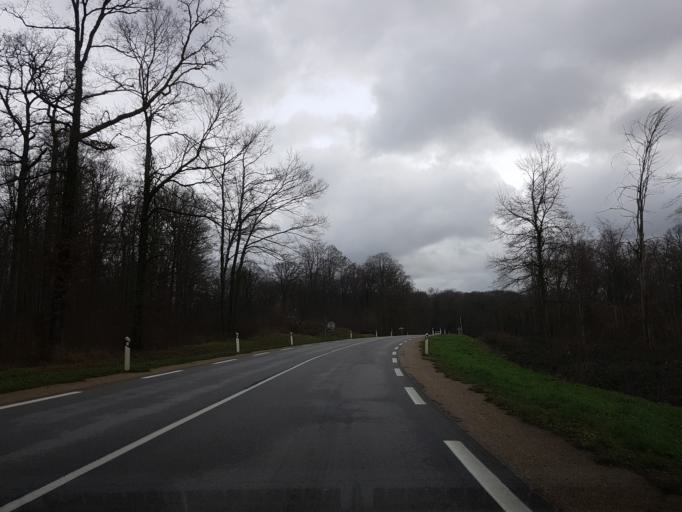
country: FR
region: Champagne-Ardenne
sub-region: Departement de la Haute-Marne
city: Fayl-Billot
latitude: 47.8072
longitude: 5.5559
